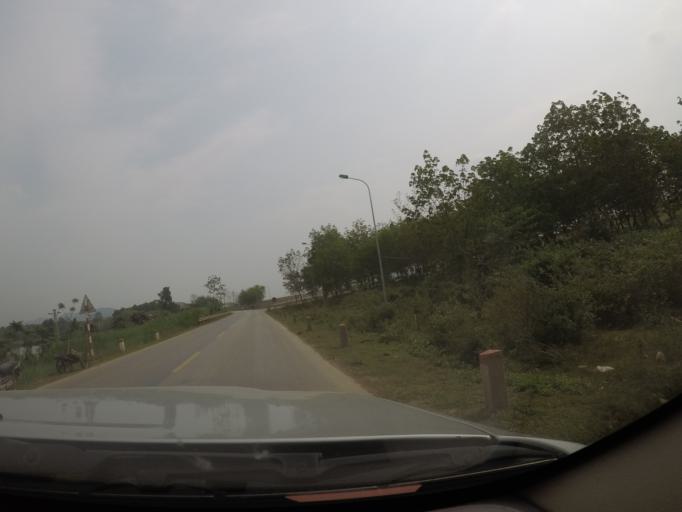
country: VN
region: Nghe An
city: Cau Giat
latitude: 19.3618
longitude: 105.4653
